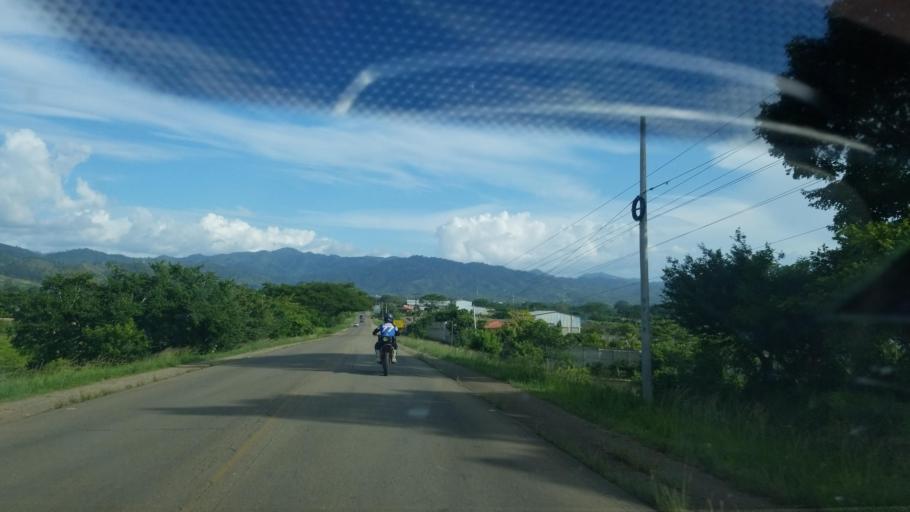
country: HN
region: El Paraiso
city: Cuyali
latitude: 13.9042
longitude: -86.5560
